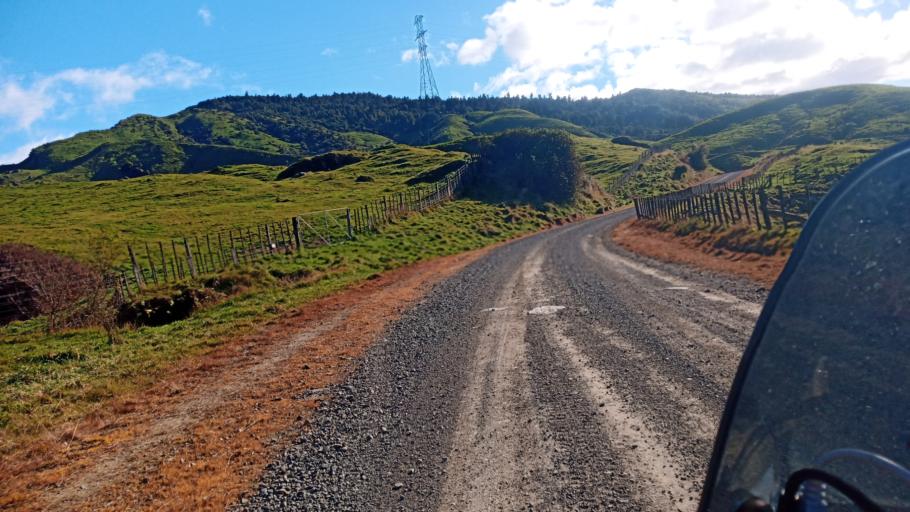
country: NZ
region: Hawke's Bay
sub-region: Wairoa District
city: Wairoa
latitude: -38.7609
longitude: 177.2648
